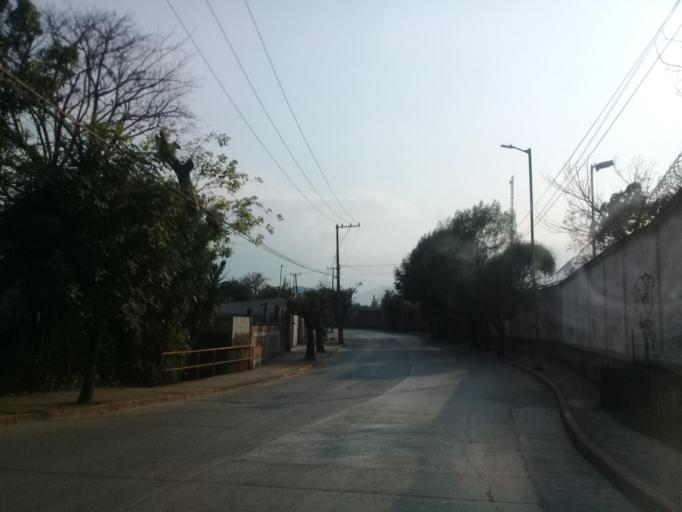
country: MX
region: Veracruz
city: Ixtac Zoquitlan
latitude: 18.8602
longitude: -97.0567
